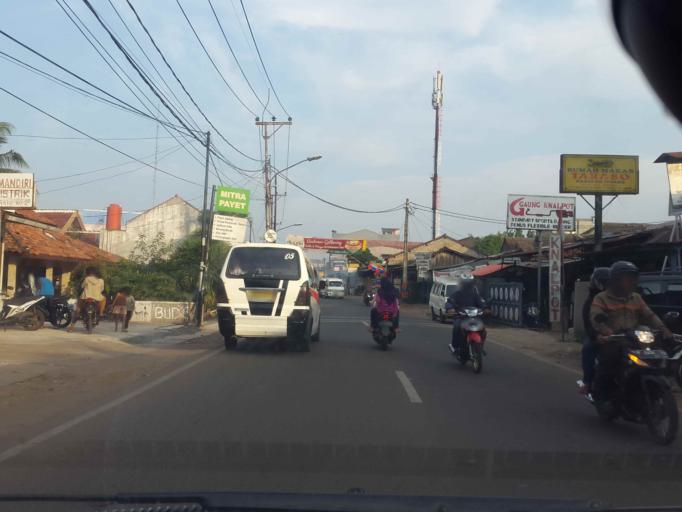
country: ID
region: Banten
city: South Tangerang
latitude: -6.2596
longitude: 106.7453
